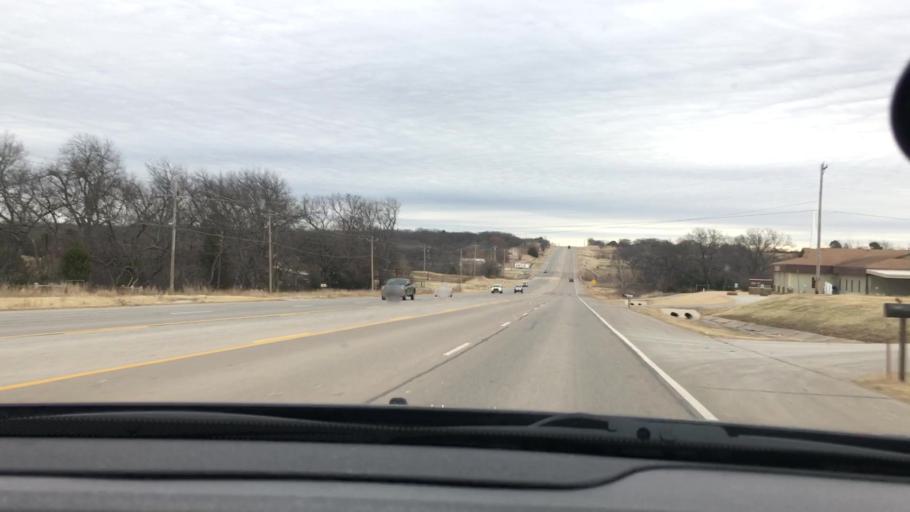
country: US
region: Oklahoma
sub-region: Carter County
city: Dickson
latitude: 34.1871
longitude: -97.0356
